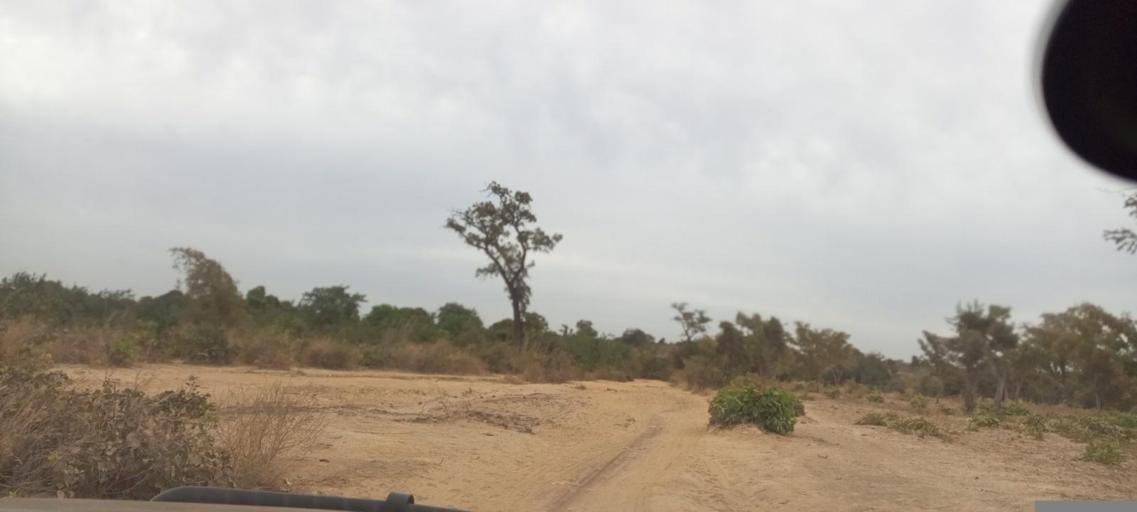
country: ML
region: Koulikoro
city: Kati
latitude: 12.7923
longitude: -8.2550
